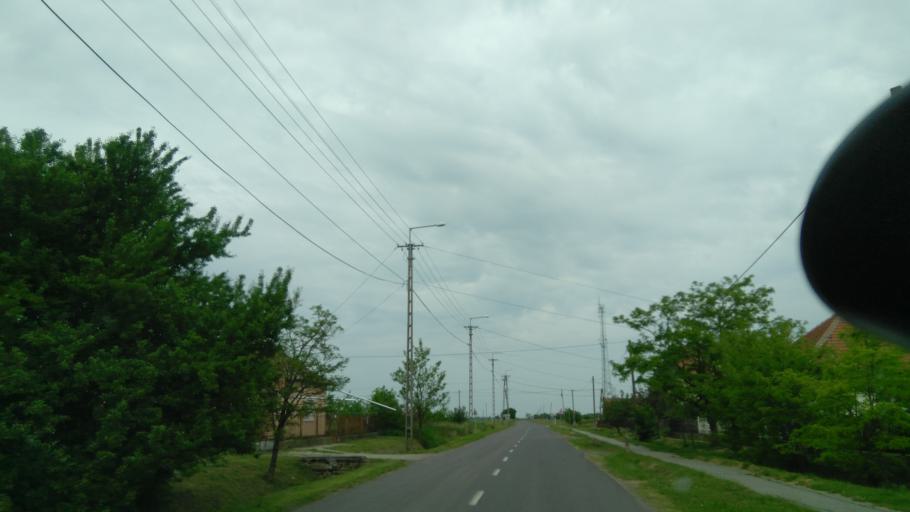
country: HU
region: Bekes
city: Szeghalom
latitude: 47.0367
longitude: 21.1579
